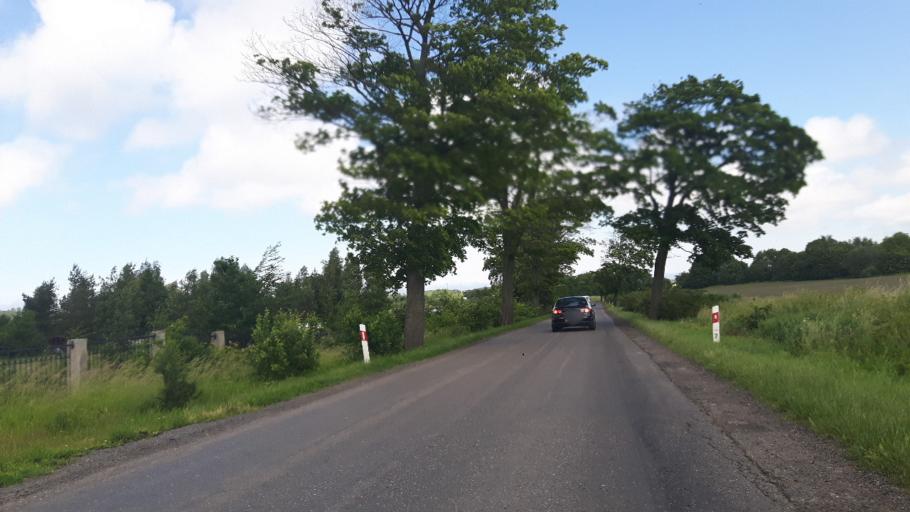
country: PL
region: Pomeranian Voivodeship
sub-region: Powiat slupski
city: Ustka
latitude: 54.5489
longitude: 16.8315
